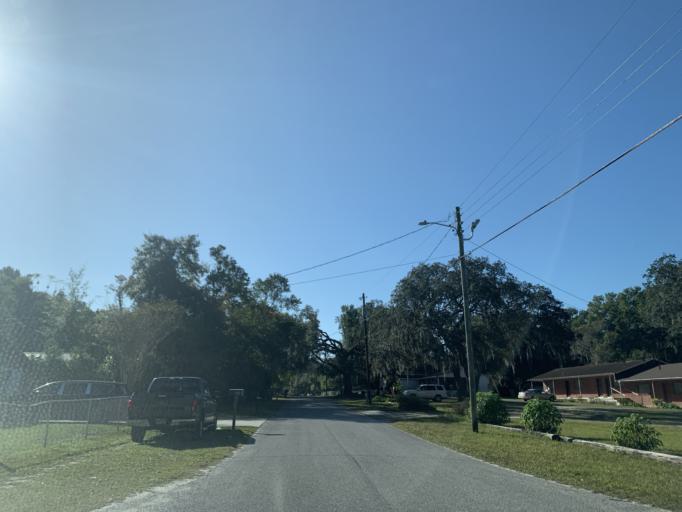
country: US
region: Florida
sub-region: Hillsborough County
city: Temple Terrace
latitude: 28.0273
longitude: -82.4154
